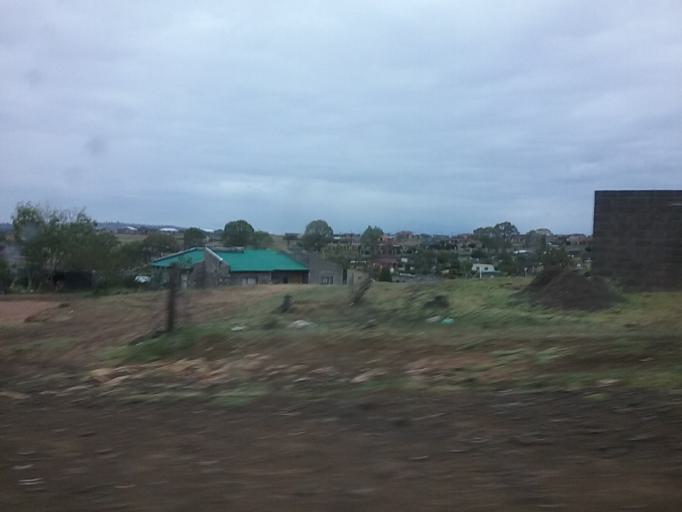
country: LS
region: Berea
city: Teyateyaneng
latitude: -29.1277
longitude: 27.7540
